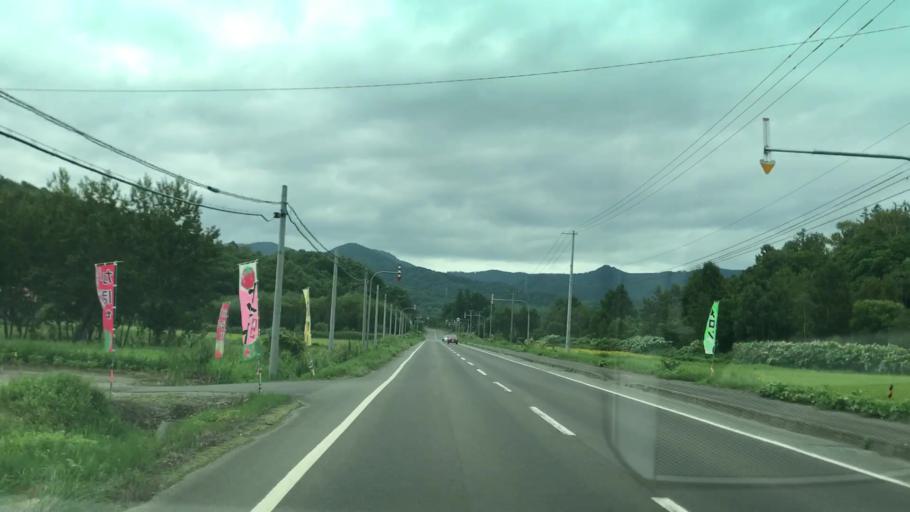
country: JP
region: Hokkaido
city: Yoichi
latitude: 43.0575
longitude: 140.8210
